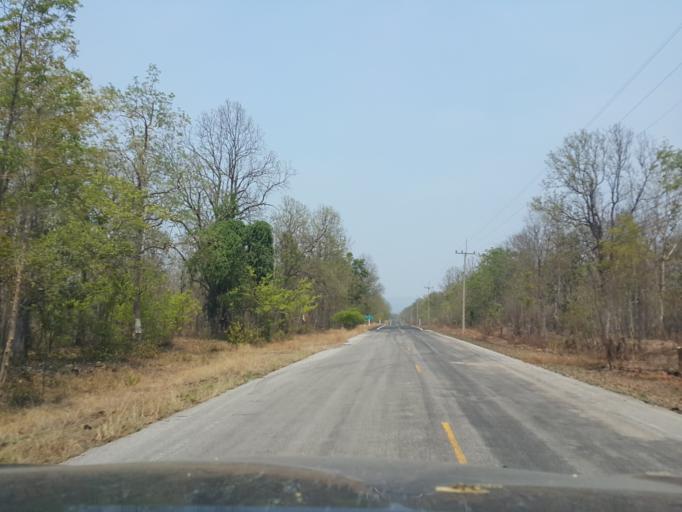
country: TH
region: Lampang
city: Mae Phrik
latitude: 17.5532
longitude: 99.1144
